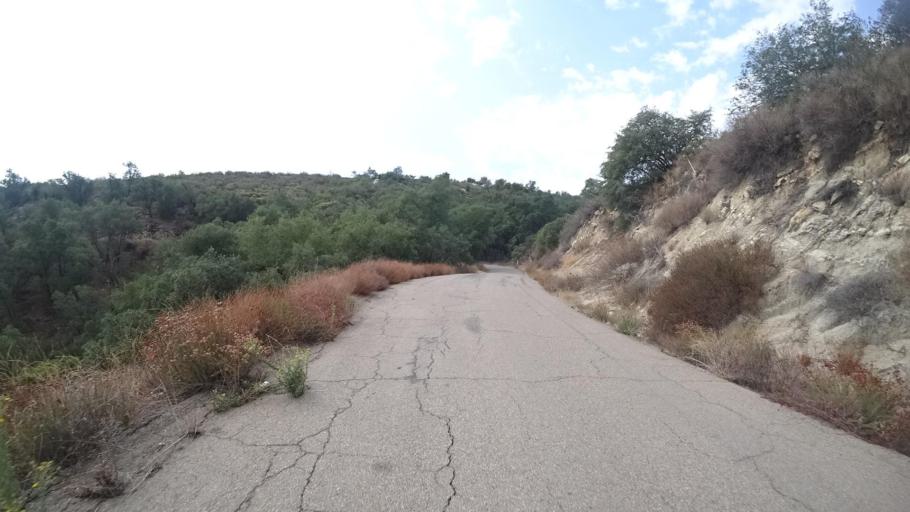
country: US
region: California
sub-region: San Diego County
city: San Diego Country Estates
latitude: 33.1079
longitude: -116.7910
